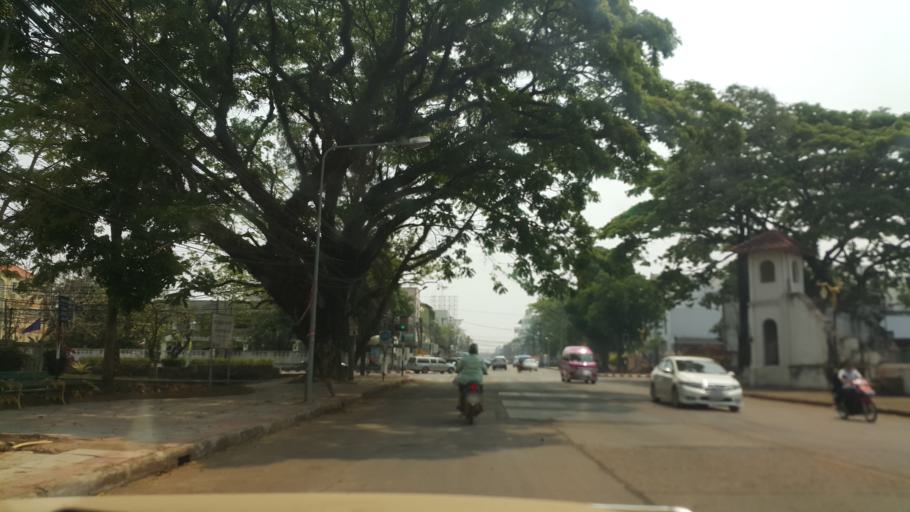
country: TH
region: Nakhon Phanom
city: Nakhon Phanom
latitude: 17.4068
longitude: 104.7815
